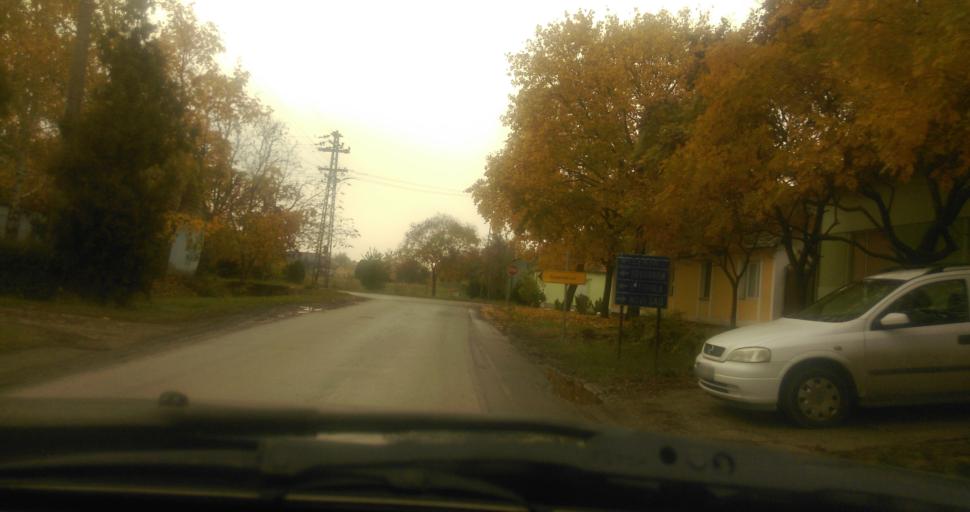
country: RS
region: Autonomna Pokrajina Vojvodina
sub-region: Juznobacki Okrug
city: Becej
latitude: 45.6142
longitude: 20.0347
